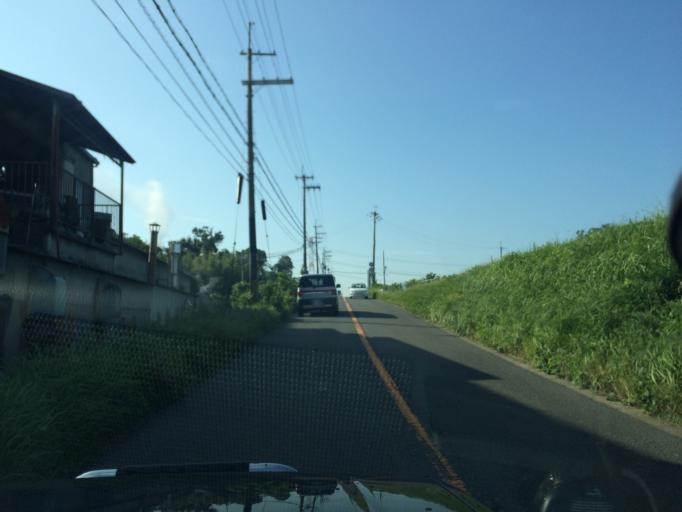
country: JP
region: Kyoto
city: Tanabe
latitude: 34.8082
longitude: 135.7888
